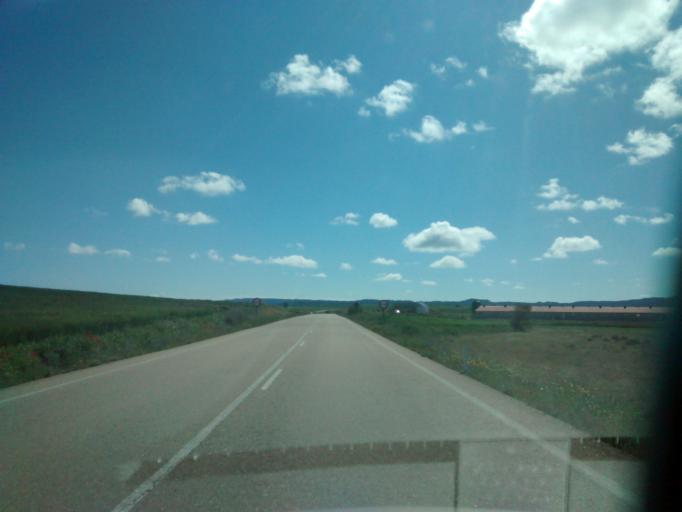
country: ES
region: Aragon
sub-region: Provincia de Zaragoza
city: Perdiguera
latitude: 41.7987
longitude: -0.6716
